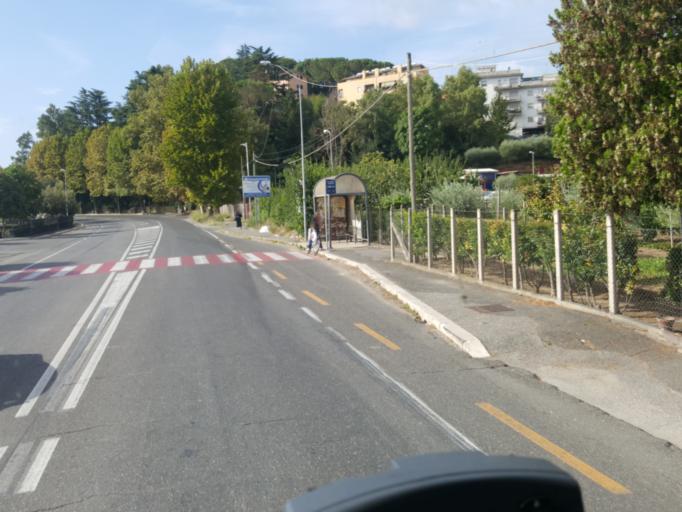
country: IT
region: Latium
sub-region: Citta metropolitana di Roma Capitale
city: Girardi-Bellavista-Terrazze
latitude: 42.1061
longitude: 12.5829
